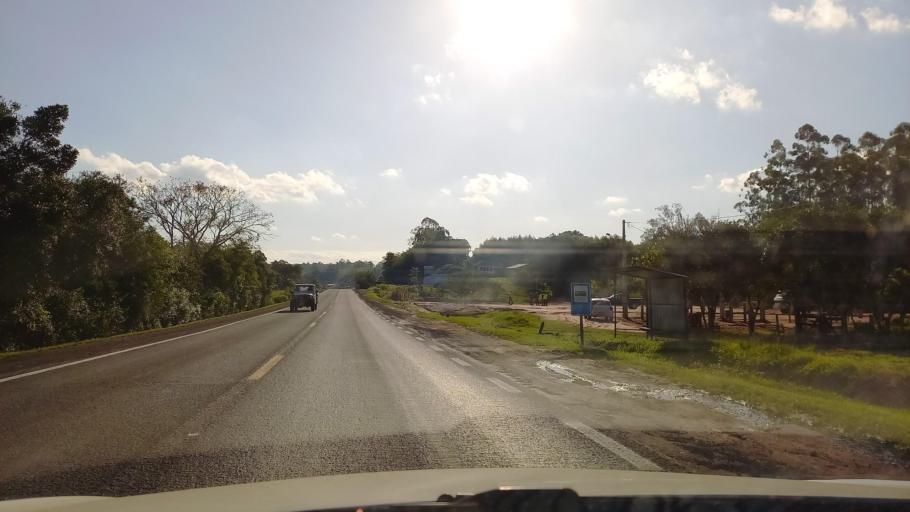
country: BR
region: Rio Grande do Sul
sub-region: Taquari
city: Taquari
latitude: -29.7108
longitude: -51.7789
